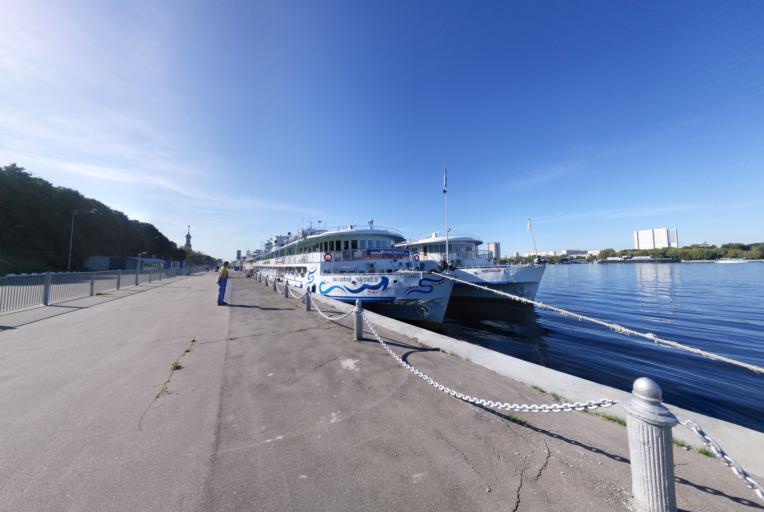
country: RU
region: Moskovskaya
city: Levoberezhnyy
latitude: 55.8500
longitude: 37.4669
